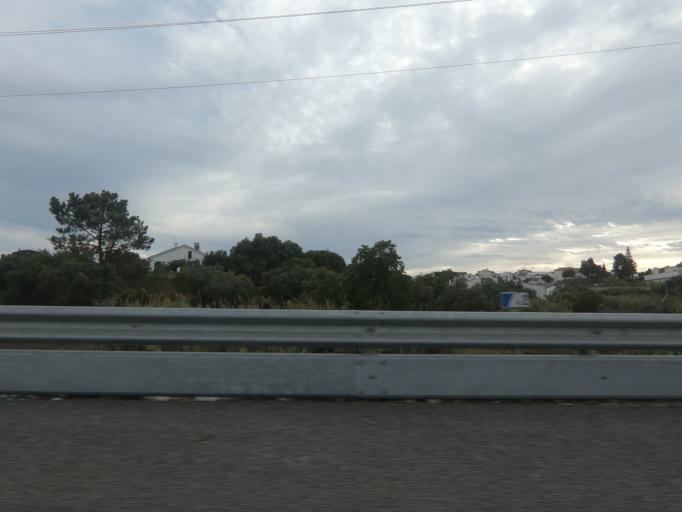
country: PT
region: Setubal
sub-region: Almada
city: Charneca
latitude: 38.6228
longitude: -9.1885
